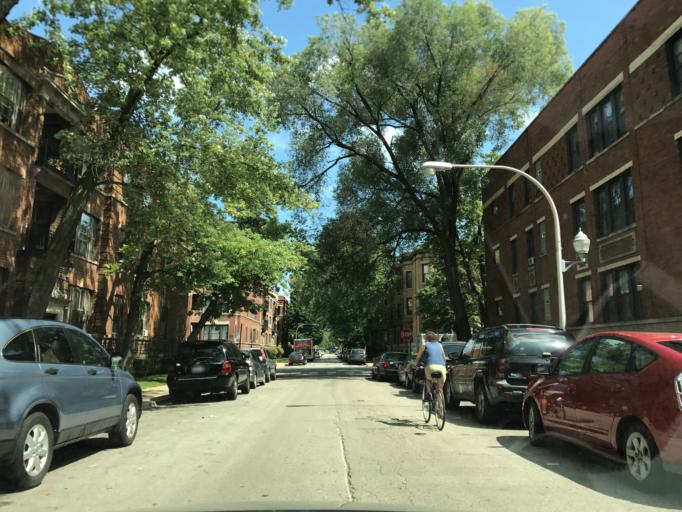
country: US
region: Illinois
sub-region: Cook County
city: Chicago
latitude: 41.7980
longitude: -87.5974
